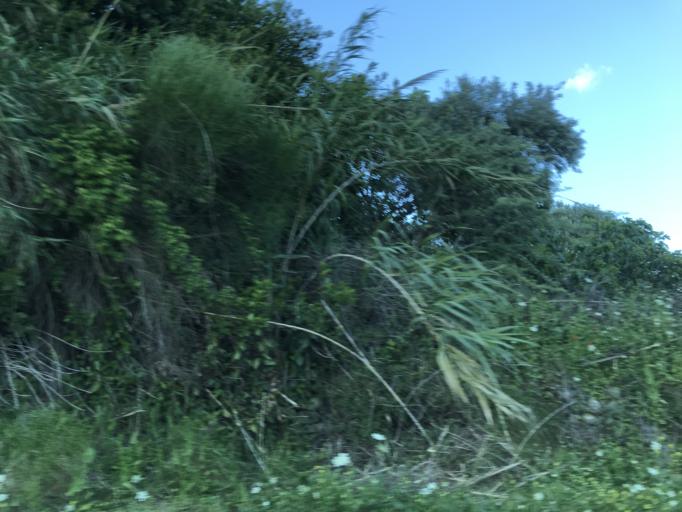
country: TR
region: Hatay
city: Buyukcat
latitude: 36.1001
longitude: 36.0624
